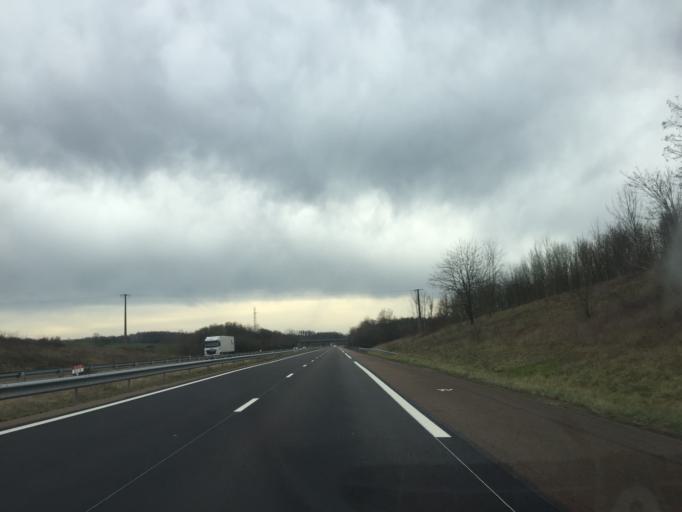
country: FR
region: Franche-Comte
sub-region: Departement du Jura
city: Bletterans
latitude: 46.7331
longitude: 5.5085
